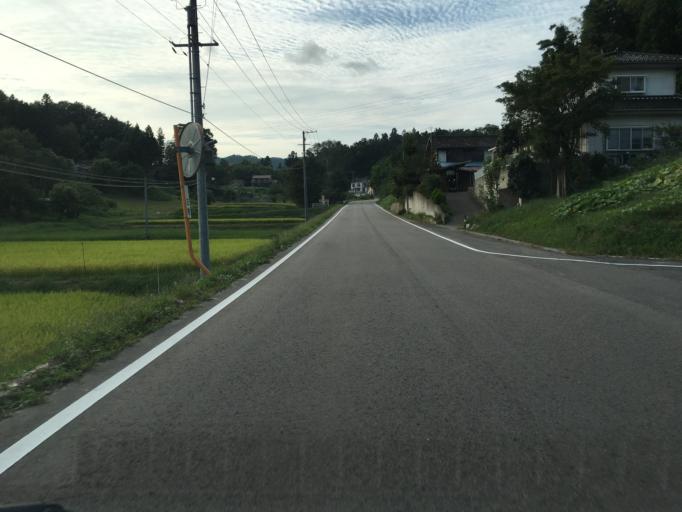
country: JP
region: Fukushima
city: Fukushima-shi
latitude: 37.6858
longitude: 140.5671
